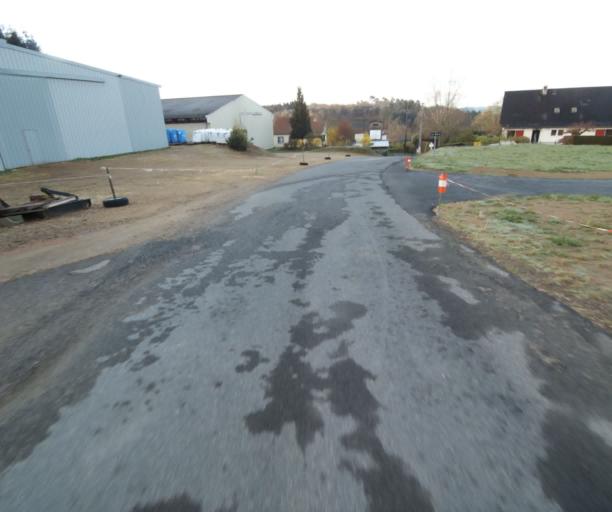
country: FR
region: Limousin
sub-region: Departement de la Correze
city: Correze
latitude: 45.3106
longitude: 1.8435
